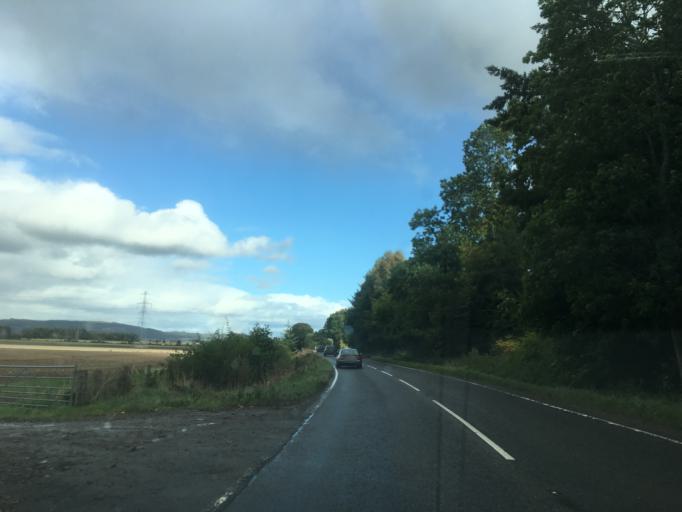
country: GB
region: Scotland
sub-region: Highland
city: Beauly
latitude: 57.4672
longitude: -4.4016
